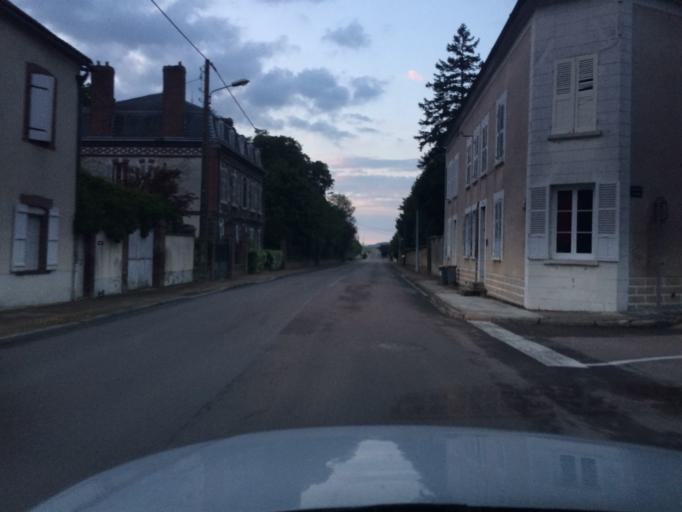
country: FR
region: Bourgogne
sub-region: Departement de l'Yonne
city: Aillant-sur-Tholon
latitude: 47.8762
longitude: 3.3502
